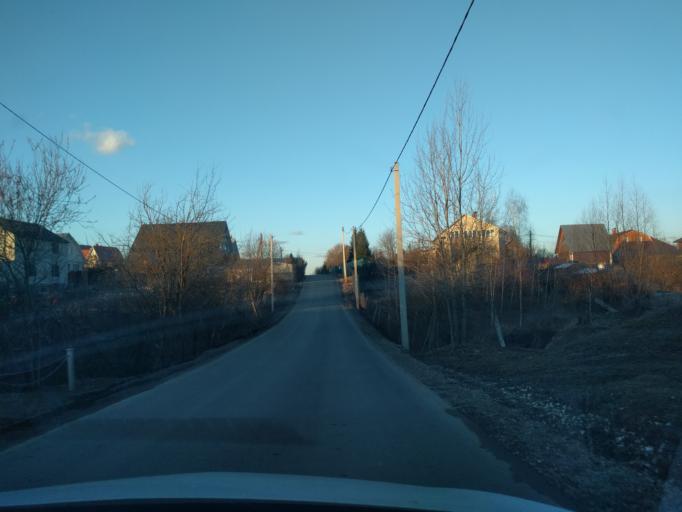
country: RU
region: Moskovskaya
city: Dubrovitsy
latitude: 55.4887
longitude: 37.4372
